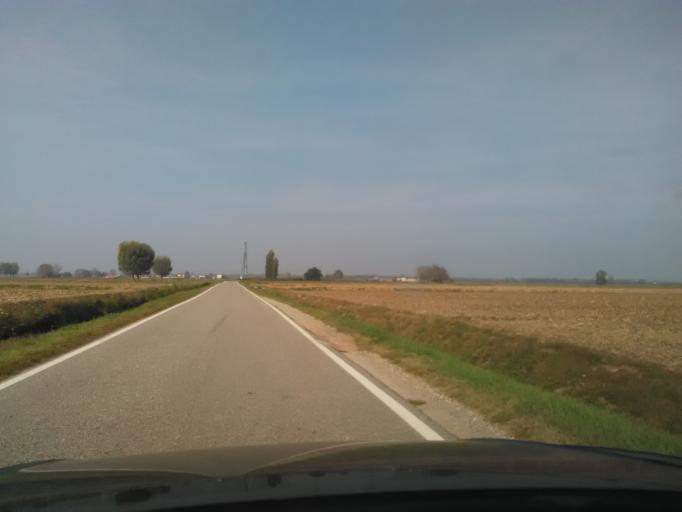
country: IT
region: Piedmont
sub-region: Provincia di Vercelli
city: Tronzano Vercellese
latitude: 45.3500
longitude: 8.1631
